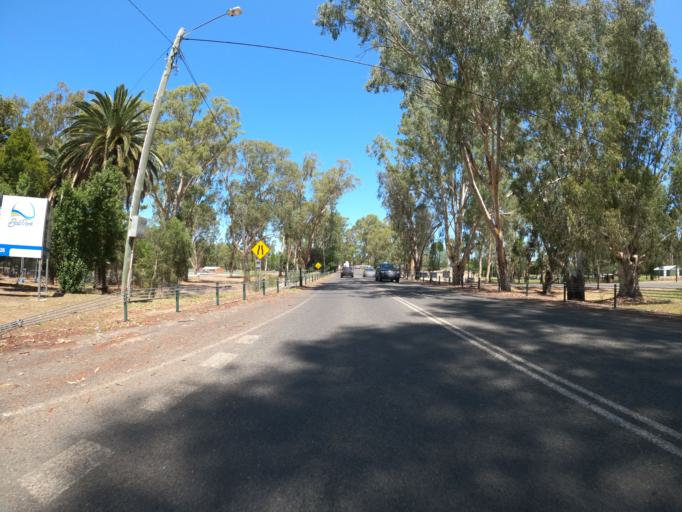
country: AU
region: New South Wales
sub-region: Corowa Shire
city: Corowa
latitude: -36.0045
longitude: 146.3946
